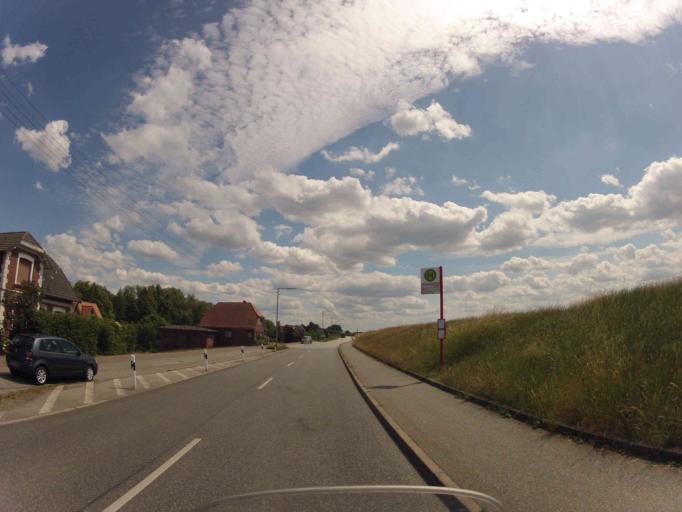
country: DE
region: Lower Saxony
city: Stelle
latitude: 53.4163
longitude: 10.1487
